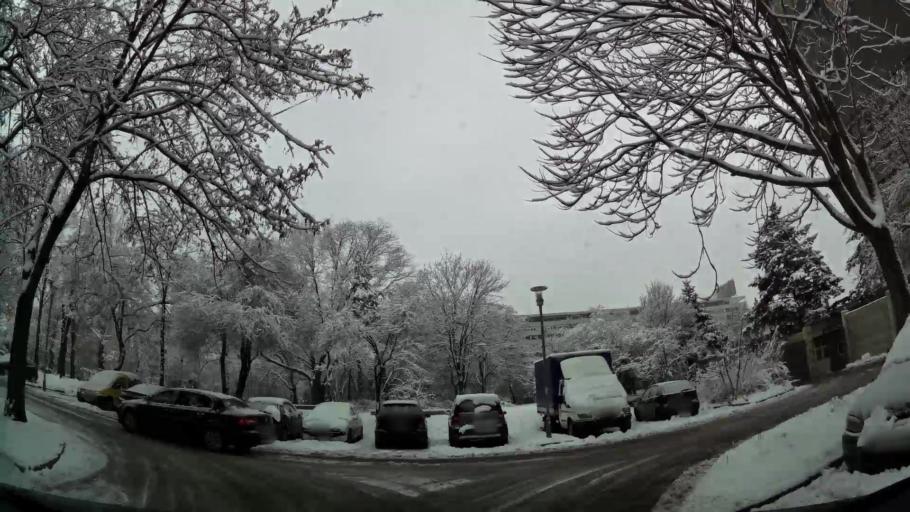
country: RS
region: Central Serbia
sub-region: Belgrade
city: Zemun
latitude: 44.8200
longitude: 20.4056
